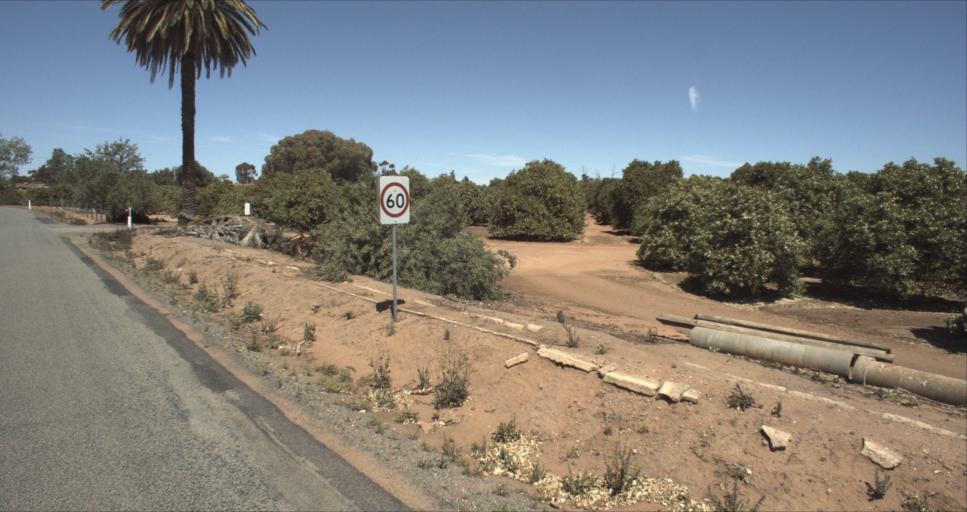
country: AU
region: New South Wales
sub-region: Leeton
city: Leeton
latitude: -34.5483
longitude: 146.3709
